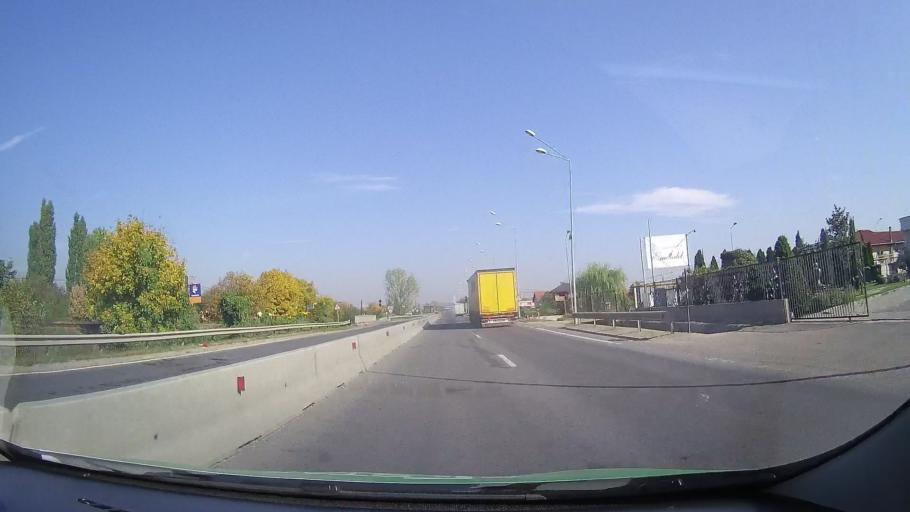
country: RO
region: Bihor
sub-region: Comuna Santandrei
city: Santandrei
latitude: 47.0521
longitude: 21.8873
